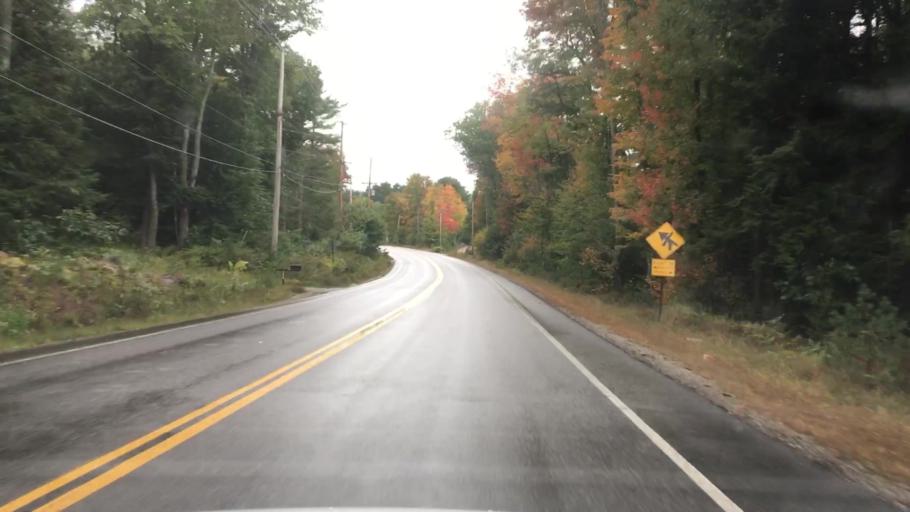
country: US
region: Maine
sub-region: Cumberland County
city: Raymond
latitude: 43.9861
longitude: -70.5531
